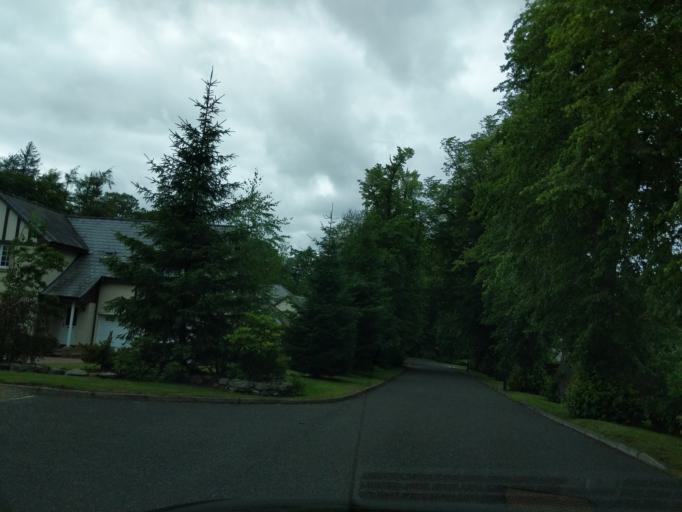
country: GB
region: Scotland
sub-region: The Scottish Borders
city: Peebles
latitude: 55.6429
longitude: -3.1977
